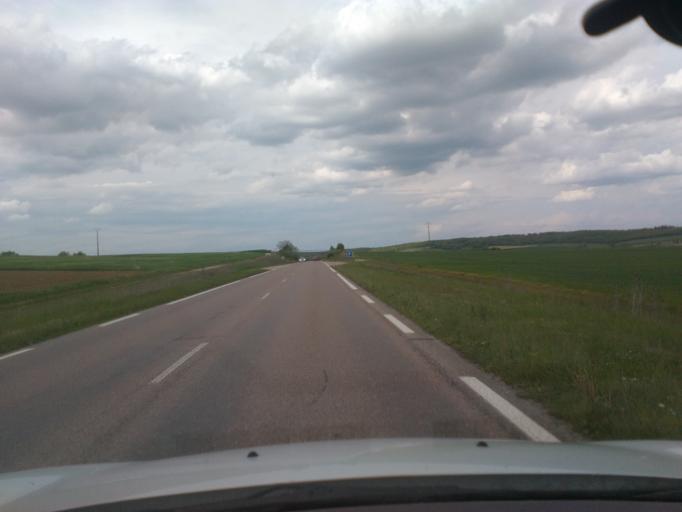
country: FR
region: Lorraine
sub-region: Departement des Vosges
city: Mirecourt
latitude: 48.2911
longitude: 6.1539
